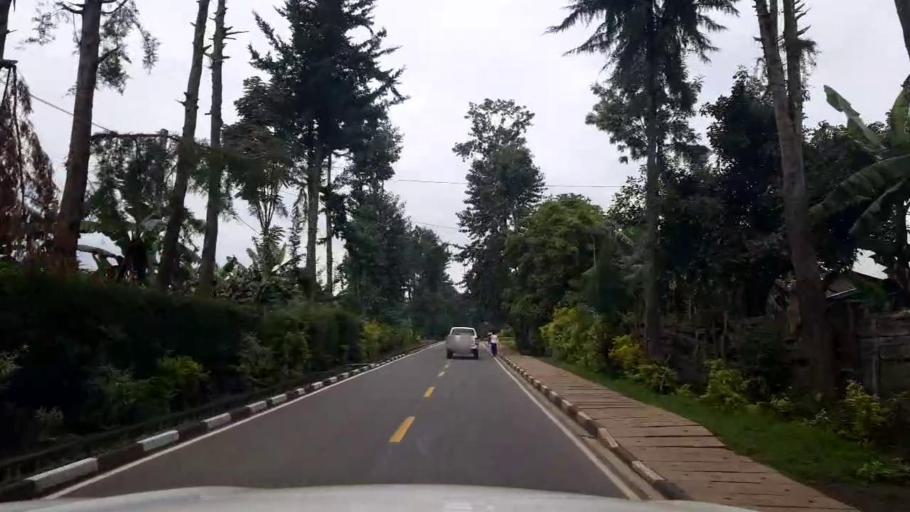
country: RW
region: Northern Province
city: Musanze
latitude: -1.4525
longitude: 29.5981
